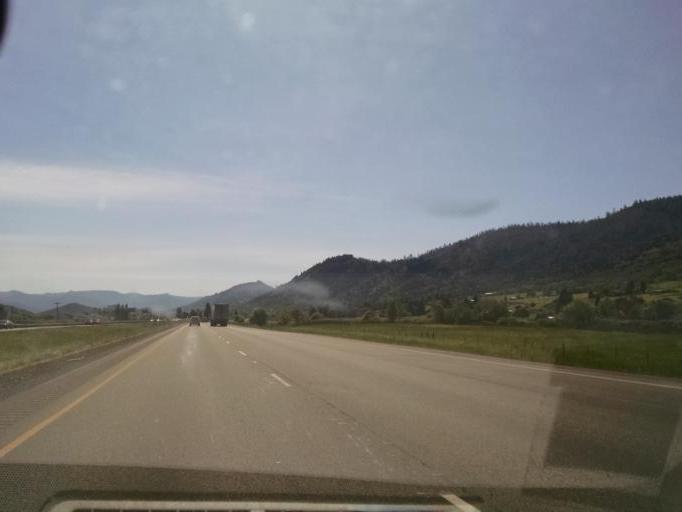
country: US
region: Oregon
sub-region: Douglas County
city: Tri-City
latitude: 43.0035
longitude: -123.3120
